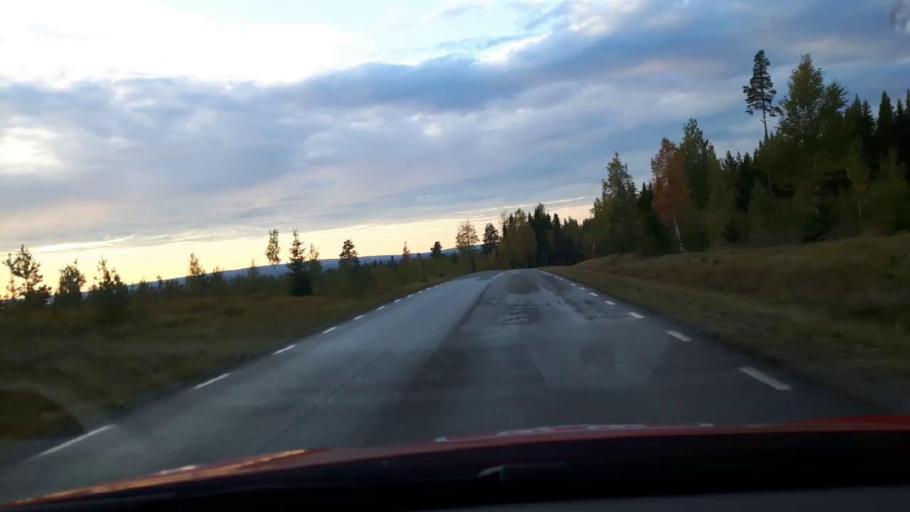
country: SE
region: Jaemtland
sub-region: OEstersunds Kommun
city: Lit
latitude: 63.3150
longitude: 15.0952
